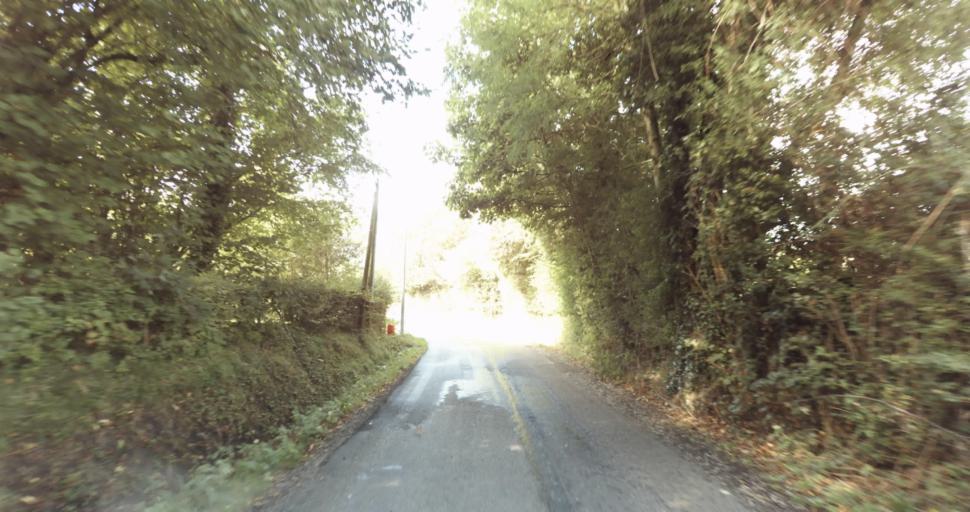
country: FR
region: Lower Normandy
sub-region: Departement de l'Orne
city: Gace
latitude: 48.7932
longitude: 0.3013
